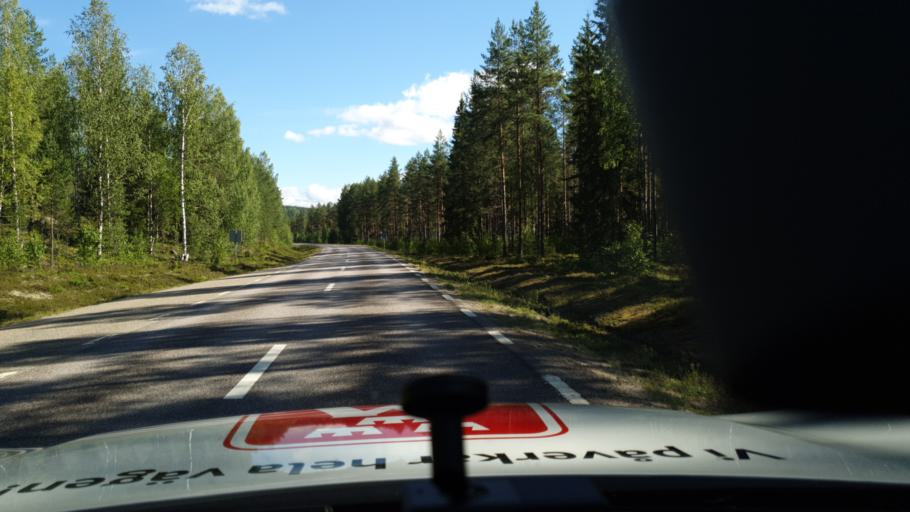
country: NO
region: Hedmark
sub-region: Trysil
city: Innbygda
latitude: 60.8742
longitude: 12.6616
